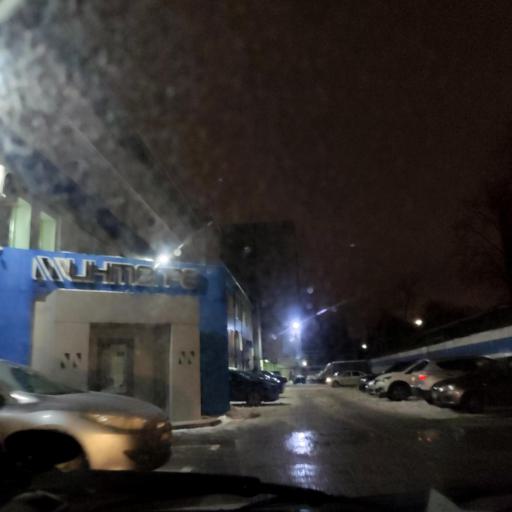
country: RU
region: Voronezj
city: Voronezh
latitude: 51.6822
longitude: 39.1809
